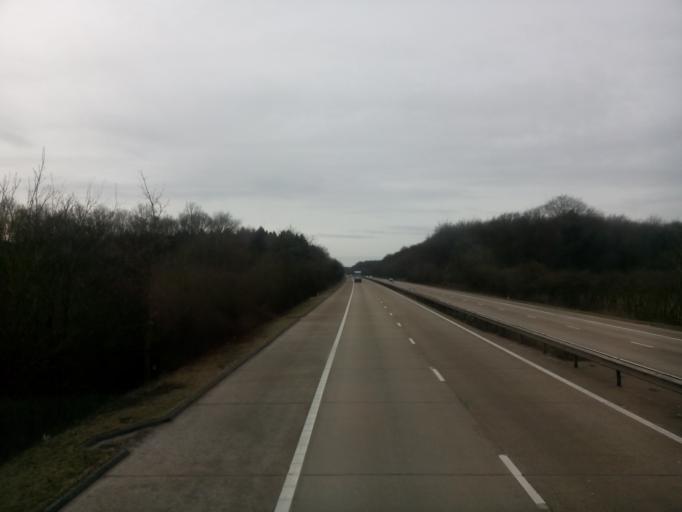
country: GB
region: England
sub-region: Hampshire
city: Kings Worthy
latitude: 51.1479
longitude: -1.2418
